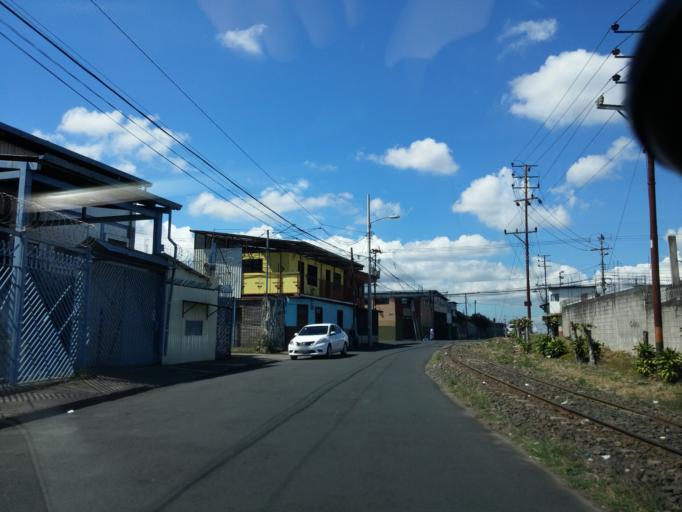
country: CR
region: San Jose
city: San Jose
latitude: 9.9250
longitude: -84.0869
